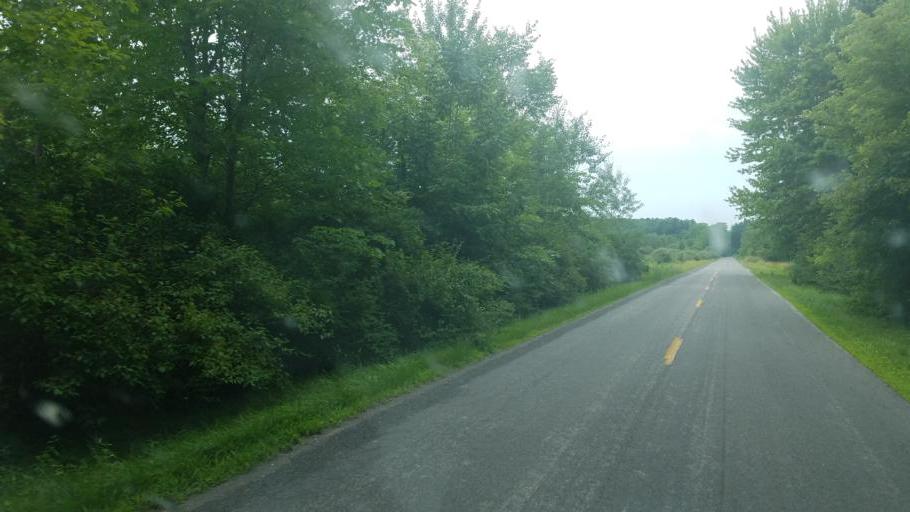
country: US
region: Ohio
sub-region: Trumbull County
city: Cortland
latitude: 41.4284
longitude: -80.7770
